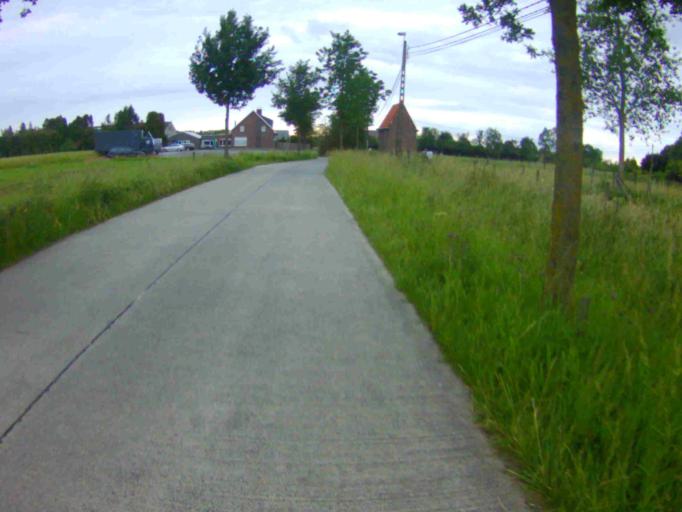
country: BE
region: Flanders
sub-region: Provincie Antwerpen
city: Lier
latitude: 51.0967
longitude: 4.5810
